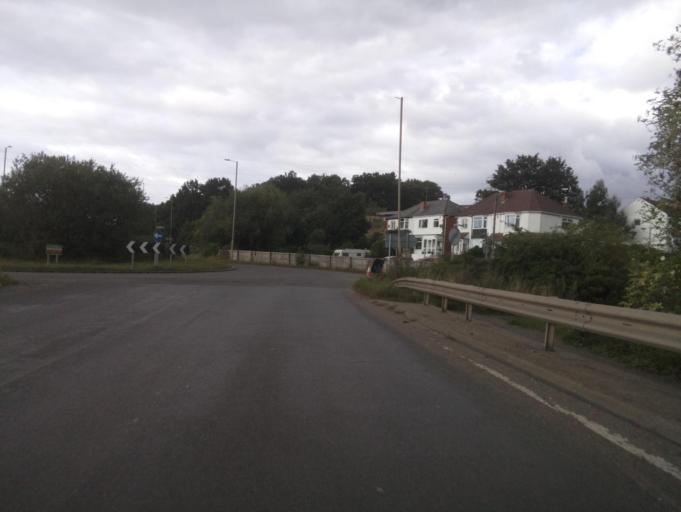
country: GB
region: England
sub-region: Warwickshire
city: Water Orton
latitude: 52.5053
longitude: -1.7117
